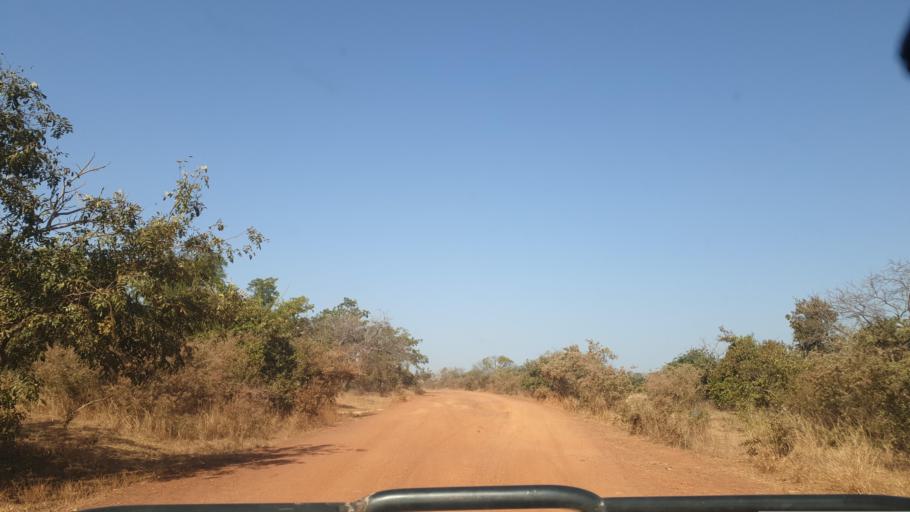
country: ML
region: Sikasso
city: Bougouni
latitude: 11.8168
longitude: -6.9384
